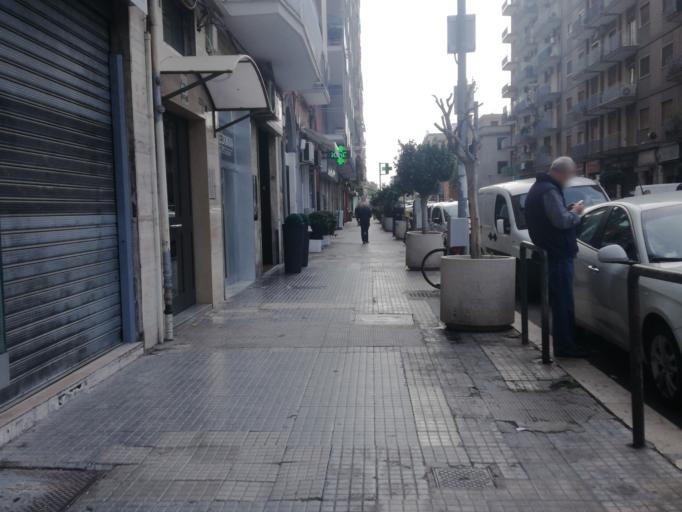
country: IT
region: Apulia
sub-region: Provincia di Bari
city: Bari
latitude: 41.1163
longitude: 16.8900
